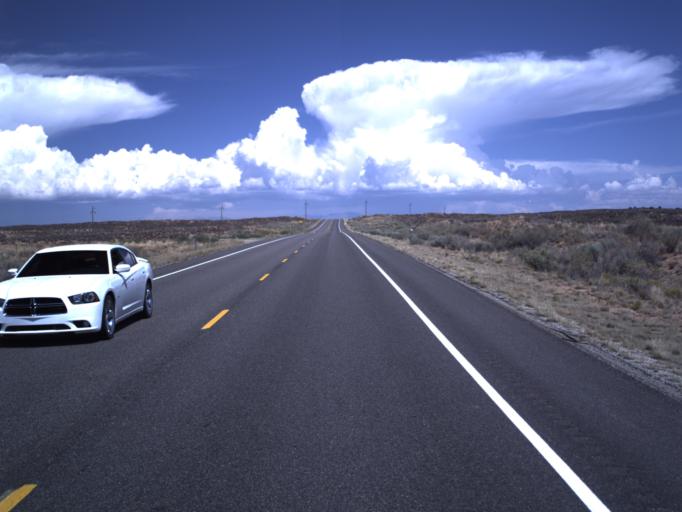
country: US
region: Utah
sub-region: San Juan County
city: Blanding
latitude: 37.3441
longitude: -109.5194
